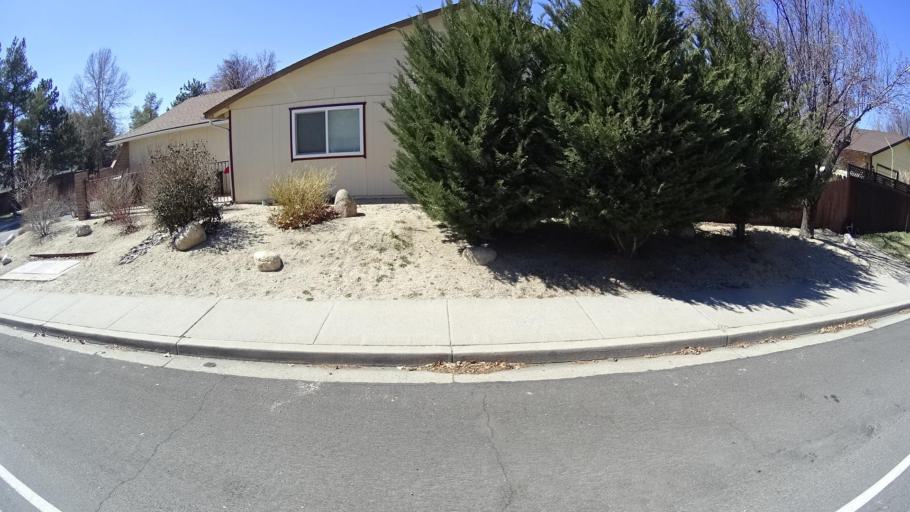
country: US
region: Nevada
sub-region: Washoe County
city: Sparks
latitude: 39.5546
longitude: -119.7156
